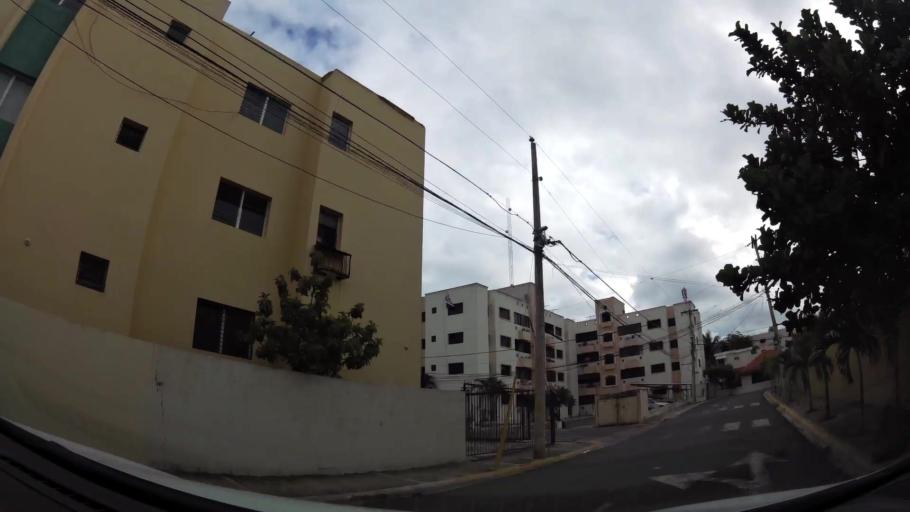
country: DO
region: Santiago
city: Santiago de los Caballeros
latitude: 19.4596
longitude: -70.6614
